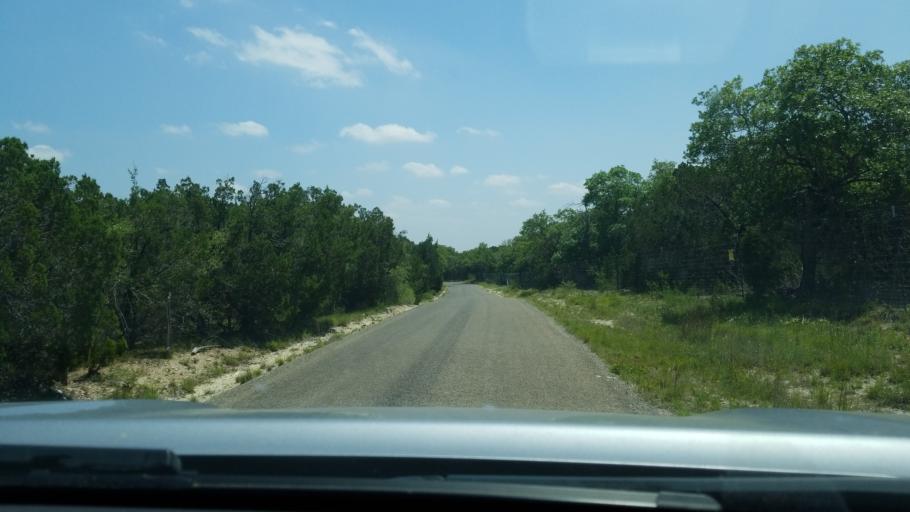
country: US
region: Texas
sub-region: Blanco County
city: Blanco
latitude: 30.0795
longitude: -98.4007
